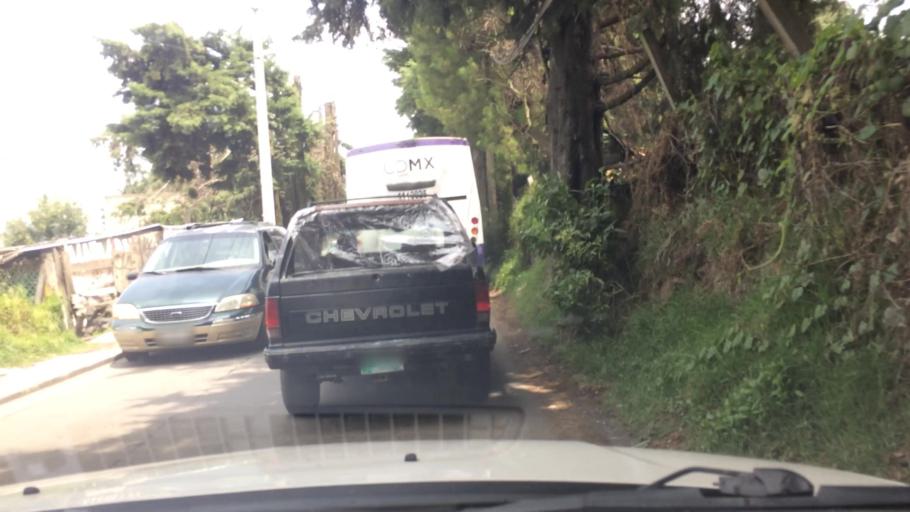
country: MX
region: Mexico City
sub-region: Tlalpan
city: Lomas de Tepemecatl
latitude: 19.2242
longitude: -99.2076
